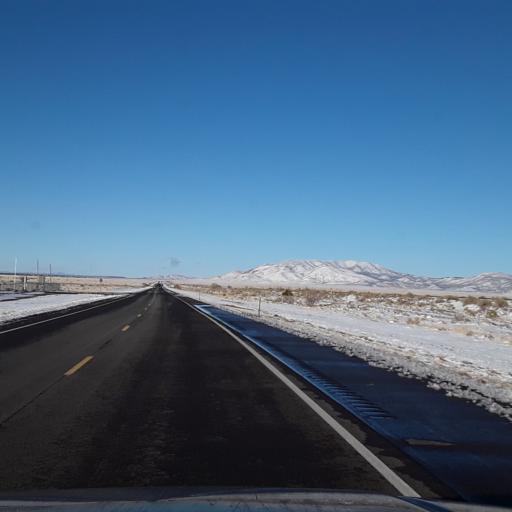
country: US
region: New Mexico
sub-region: Lincoln County
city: Carrizozo
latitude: 33.6546
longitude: -105.8629
